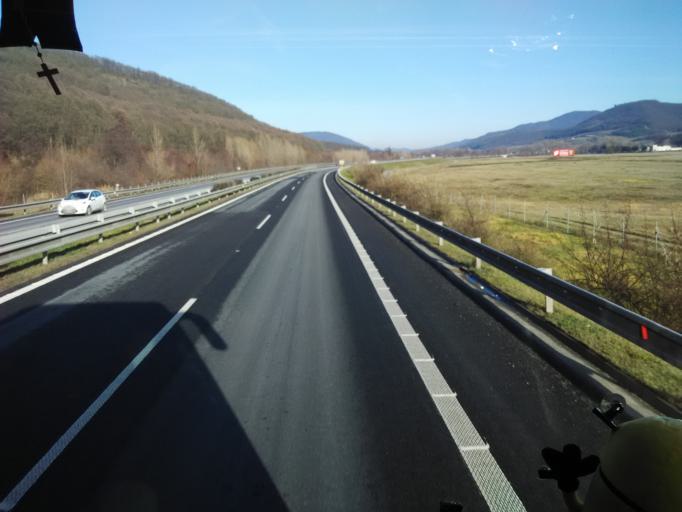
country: SK
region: Banskobystricky
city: Nova Bana
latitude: 48.3639
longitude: 18.5824
